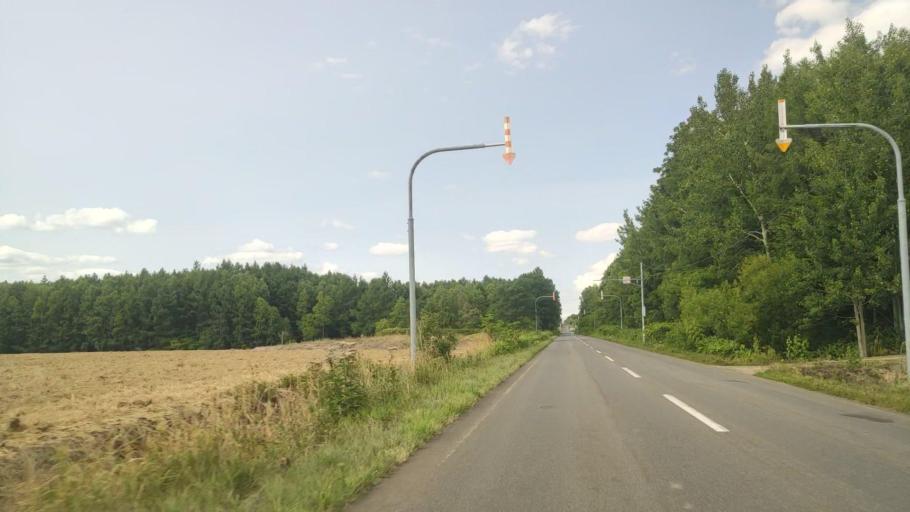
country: JP
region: Hokkaido
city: Nayoro
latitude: 44.2420
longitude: 142.4157
